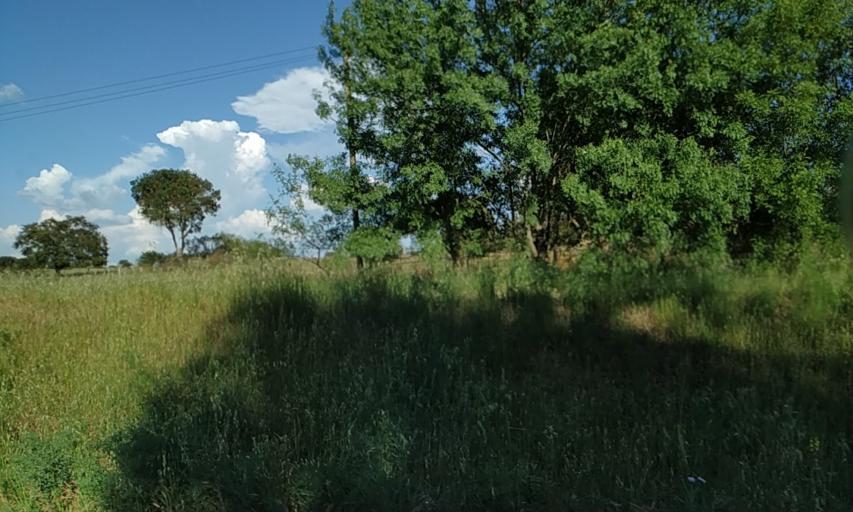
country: PT
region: Portalegre
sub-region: Fronteira
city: Fronteira
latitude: 39.0176
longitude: -7.4652
